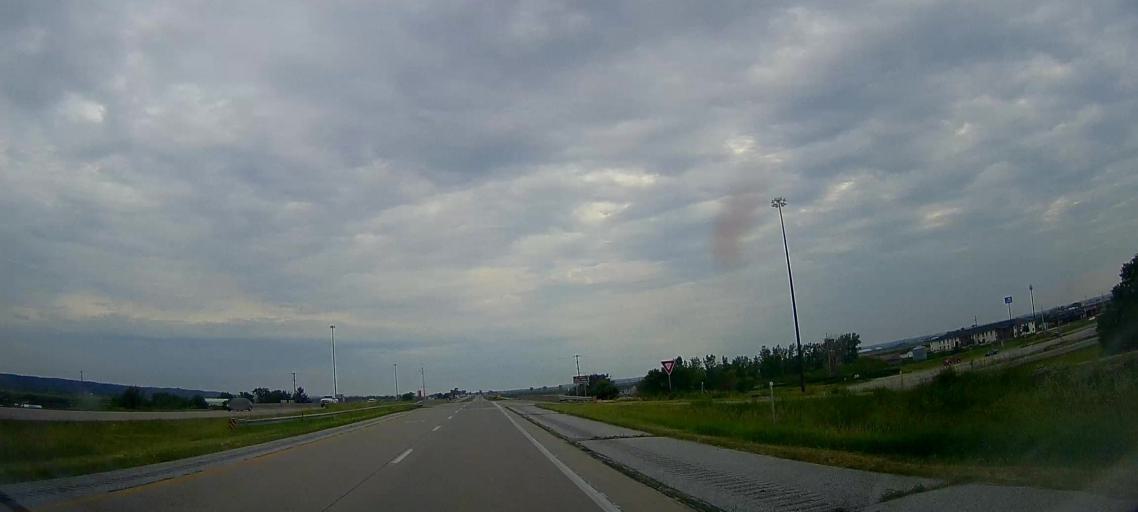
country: US
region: Iowa
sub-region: Harrison County
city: Missouri Valley
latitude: 41.5507
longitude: -95.9176
